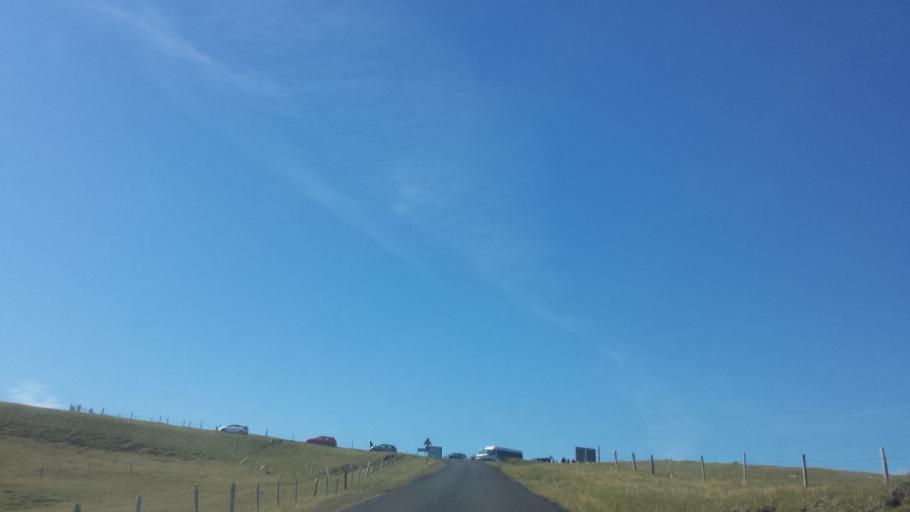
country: IS
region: South
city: Vestmannaeyjar
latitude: 63.4004
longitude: -20.2847
